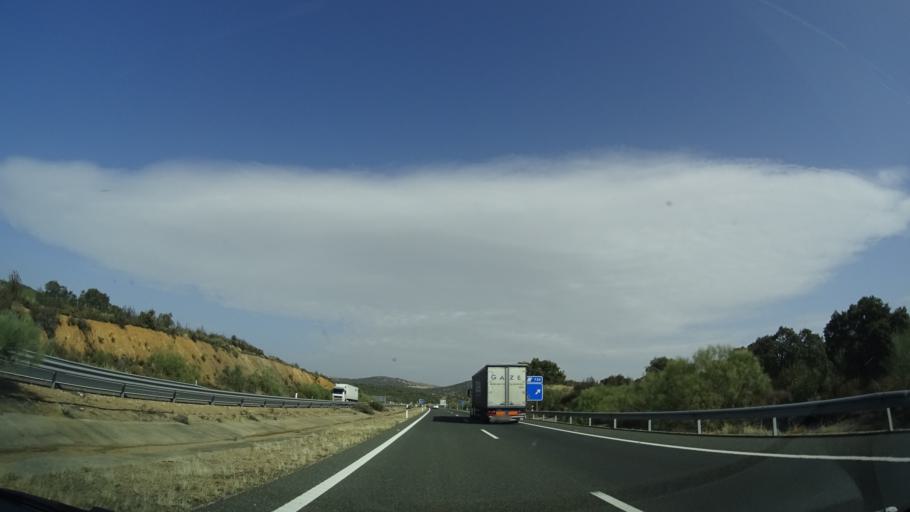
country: ES
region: Extremadura
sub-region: Provincia de Badajoz
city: Monesterio
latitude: 38.0196
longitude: -6.2244
